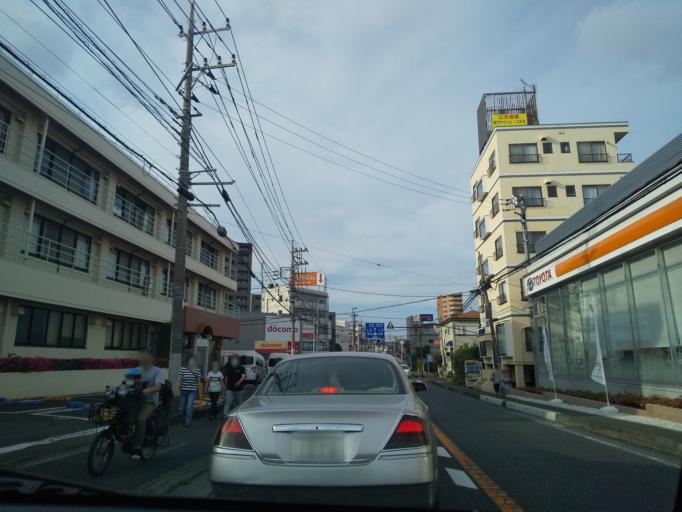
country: JP
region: Kanagawa
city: Zama
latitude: 35.5058
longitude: 139.4122
